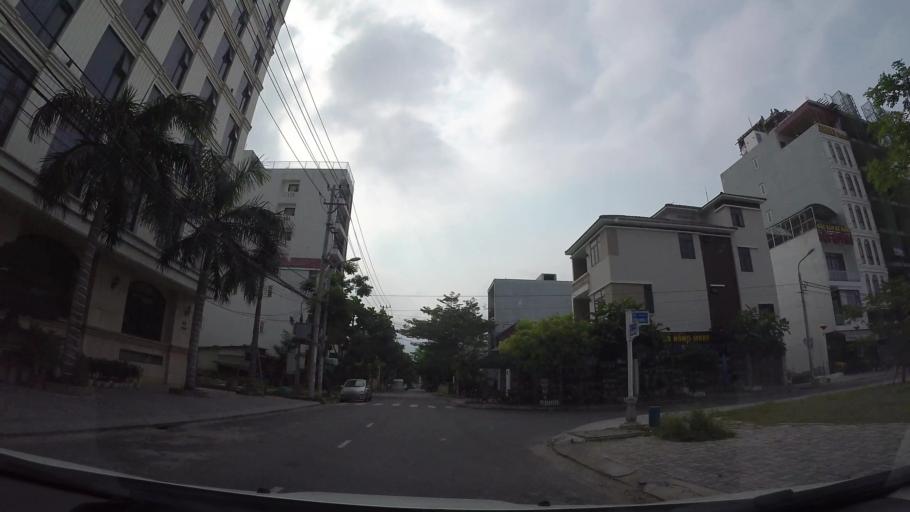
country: VN
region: Da Nang
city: Son Tra
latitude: 16.0755
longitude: 108.2420
